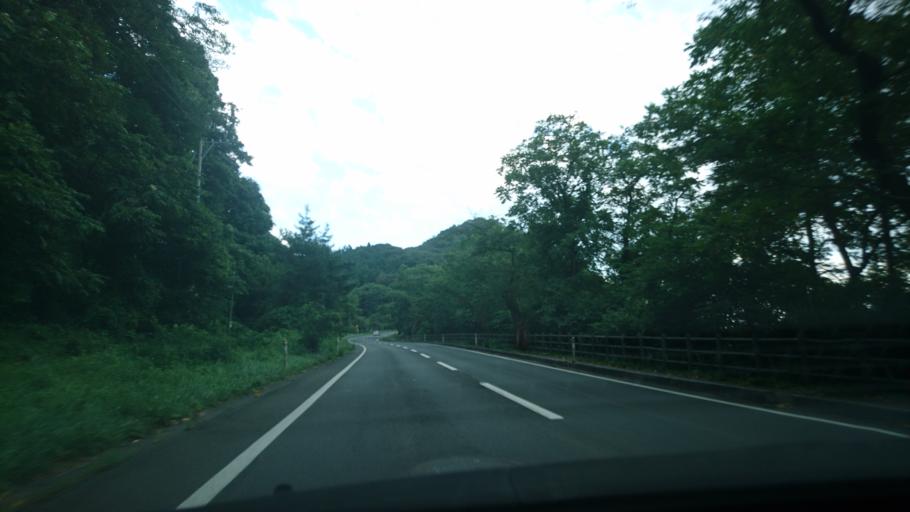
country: JP
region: Iwate
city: Kitakami
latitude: 39.2681
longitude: 141.1260
